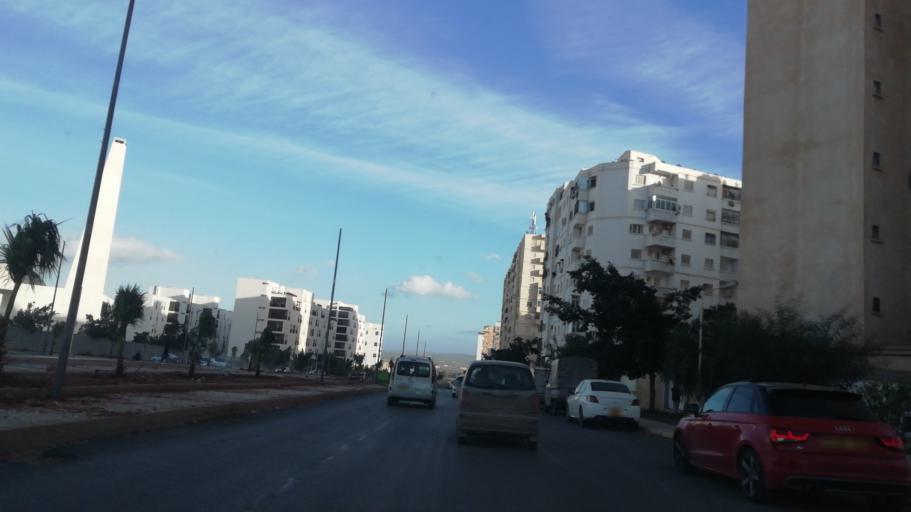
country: DZ
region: Oran
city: Bir el Djir
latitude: 35.7068
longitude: -0.5595
